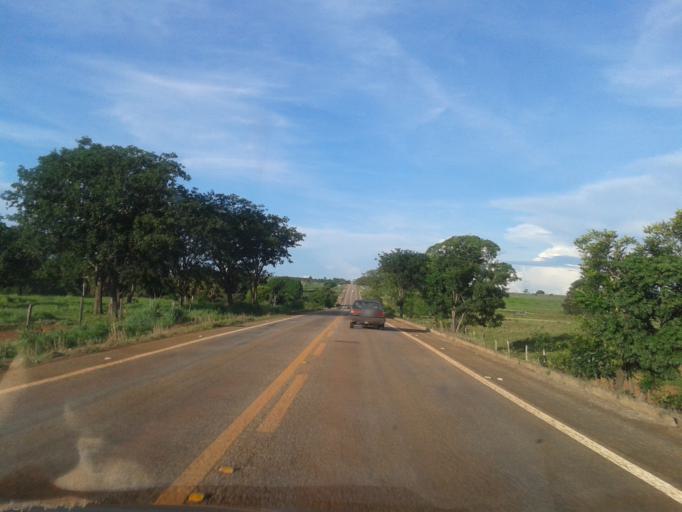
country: BR
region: Goias
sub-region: Sao Miguel Do Araguaia
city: Sao Miguel do Araguaia
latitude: -13.4407
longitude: -50.2887
